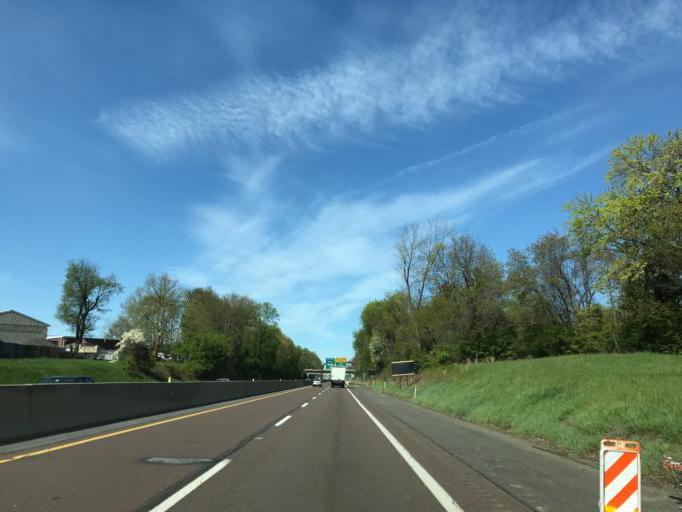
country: US
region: Pennsylvania
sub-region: Bucks County
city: Hulmeville
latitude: 40.1286
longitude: -74.9192
